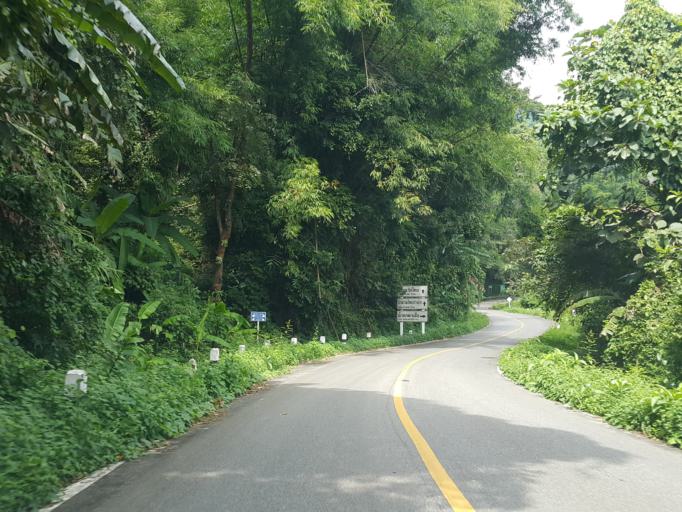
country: TH
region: Mae Hong Son
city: Mae Hong Son
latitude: 19.4889
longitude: 97.9576
